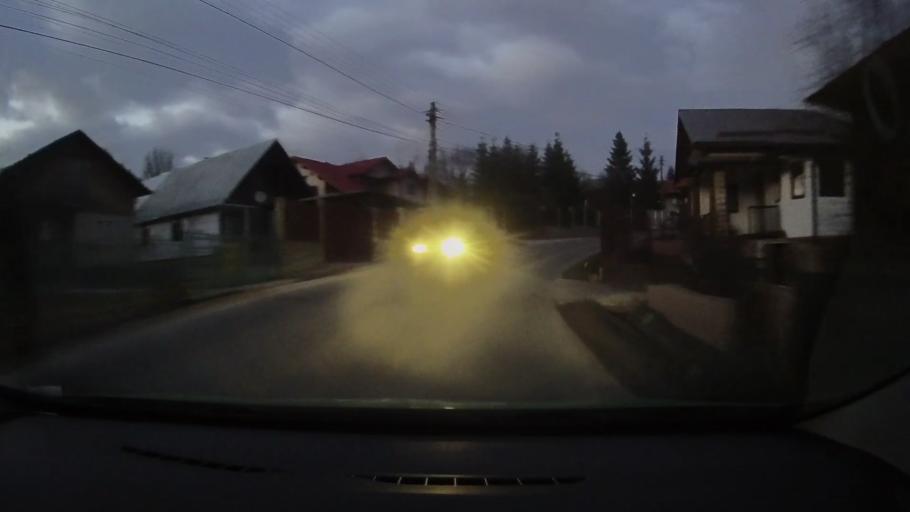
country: RO
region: Prahova
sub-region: Comuna Poiana Campina
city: Poiana Campina
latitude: 45.1243
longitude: 25.6758
